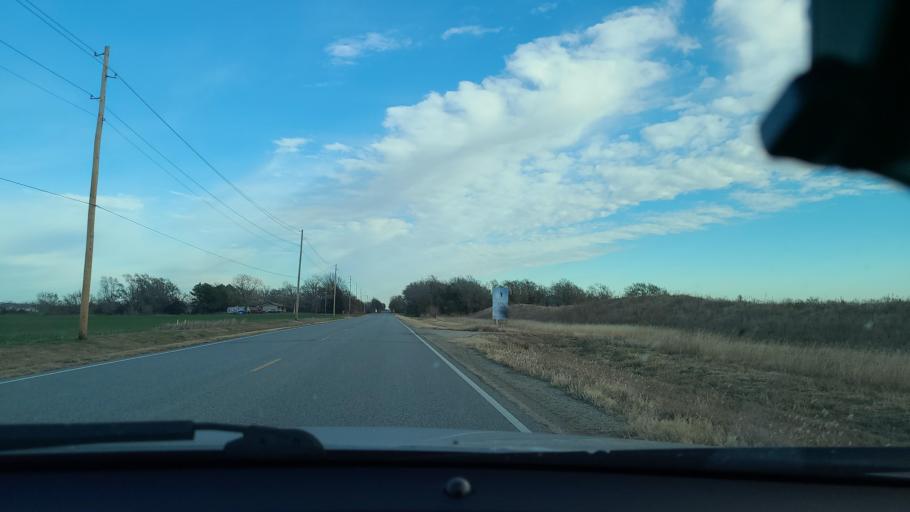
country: US
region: Kansas
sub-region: Sedgwick County
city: Goddard
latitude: 37.6496
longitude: -97.5584
